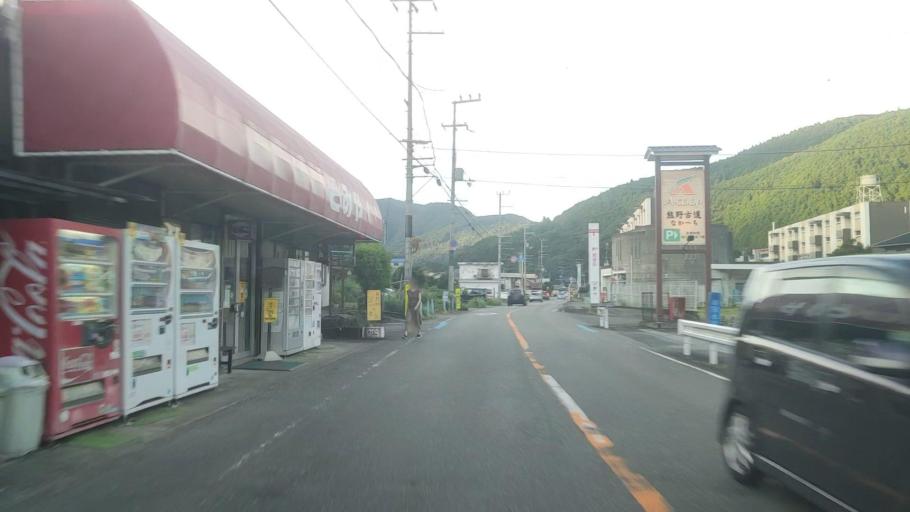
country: JP
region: Wakayama
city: Tanabe
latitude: 33.7920
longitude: 135.5167
